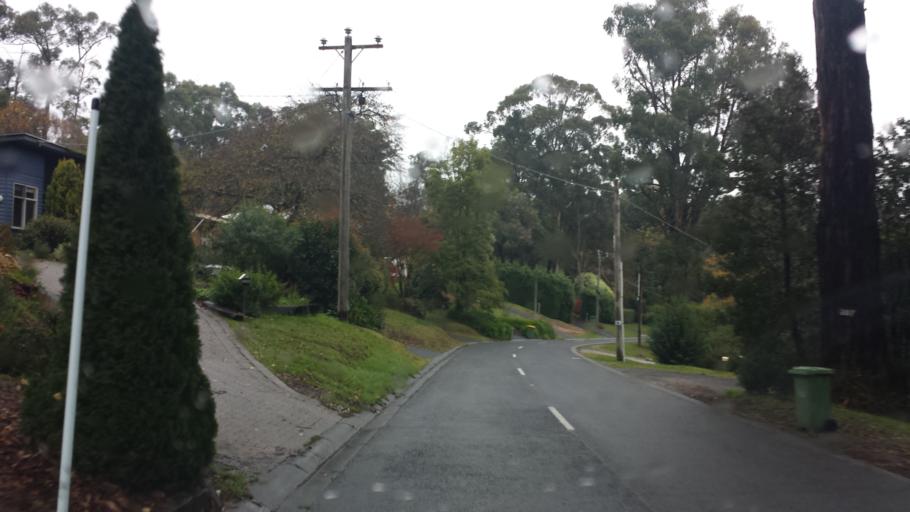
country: AU
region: Victoria
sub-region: Yarra Ranges
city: Monbulk
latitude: -37.8776
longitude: 145.4083
